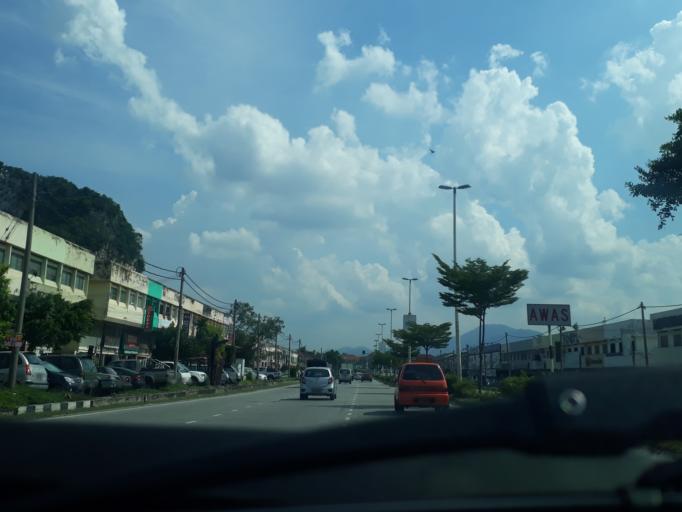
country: MY
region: Perak
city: Ipoh
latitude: 4.6432
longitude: 101.0970
